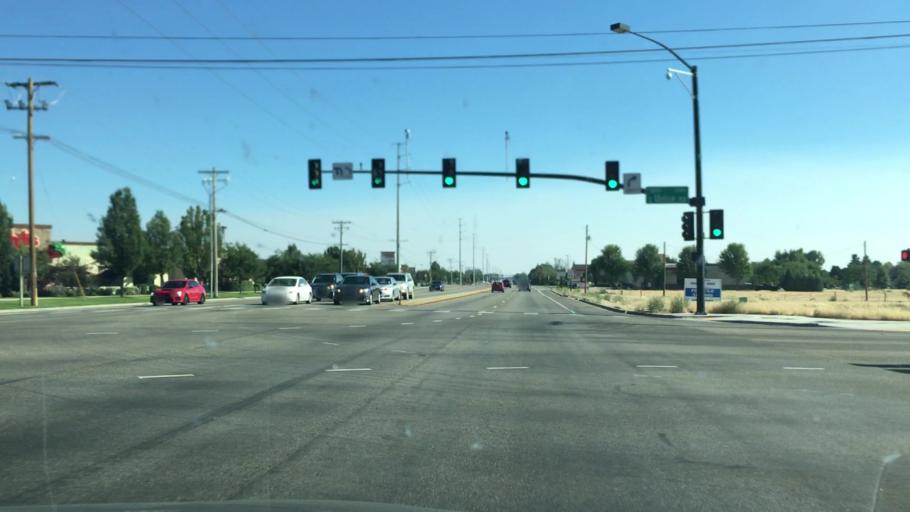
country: US
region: Idaho
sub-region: Ada County
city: Meridian
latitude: 43.6339
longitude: -116.3545
